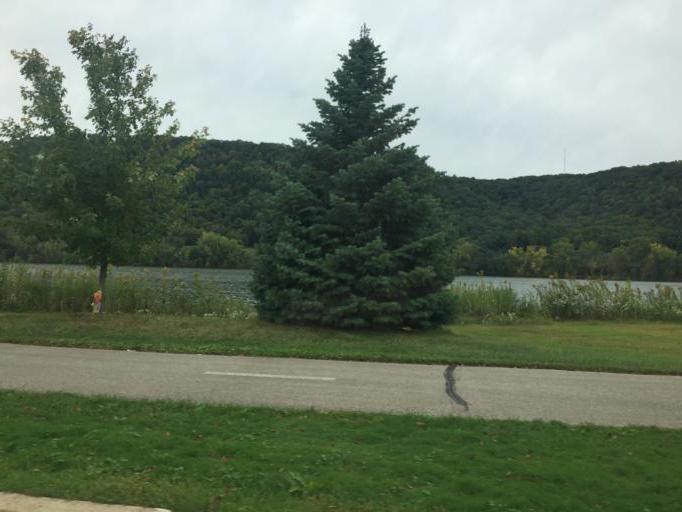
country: US
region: Minnesota
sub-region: Winona County
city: Winona
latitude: 44.0403
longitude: -91.6432
